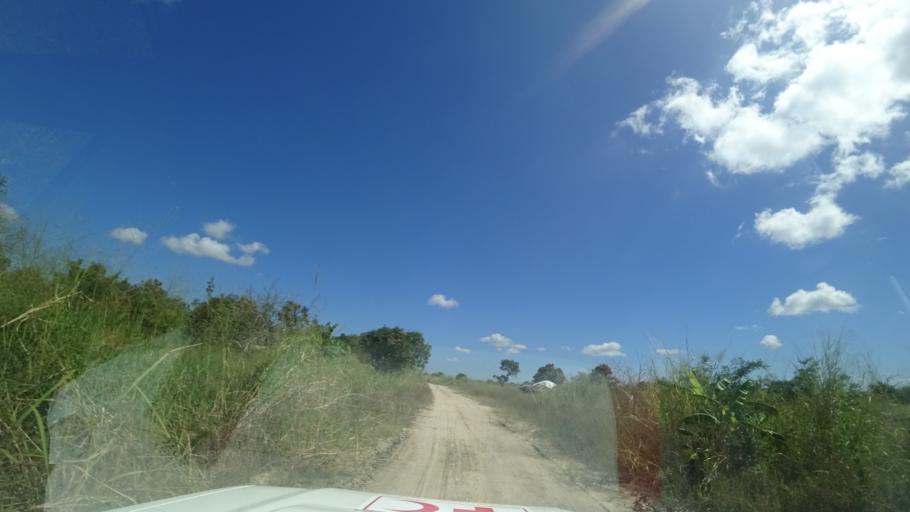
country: MZ
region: Sofala
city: Dondo
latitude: -19.3873
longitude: 34.5860
